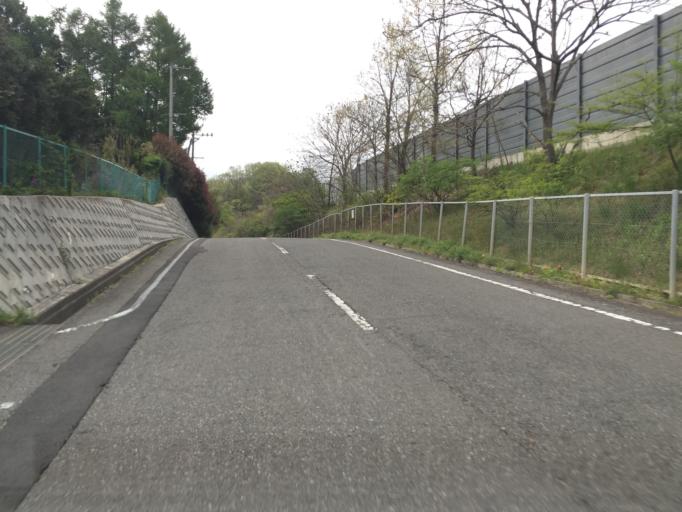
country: JP
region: Fukushima
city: Nihommatsu
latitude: 37.6462
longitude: 140.4331
